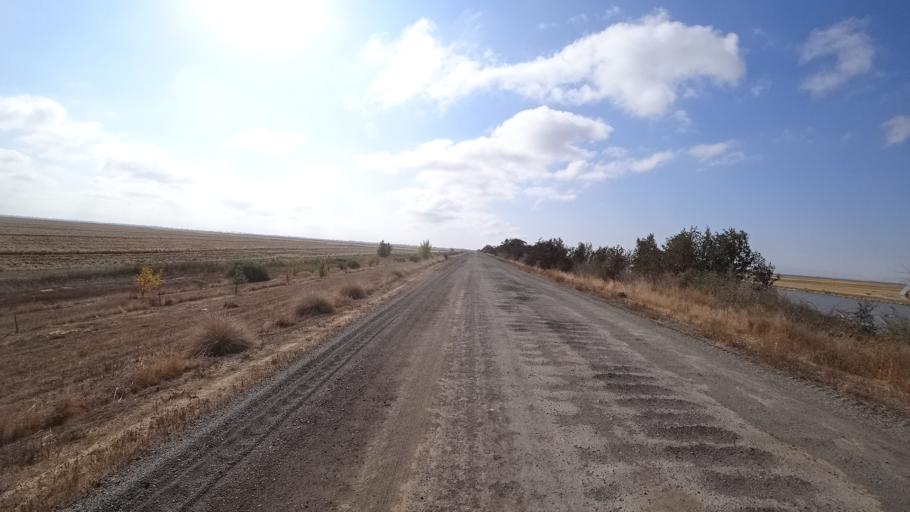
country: US
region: California
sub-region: Yolo County
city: Woodland
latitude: 38.8465
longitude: -121.7901
